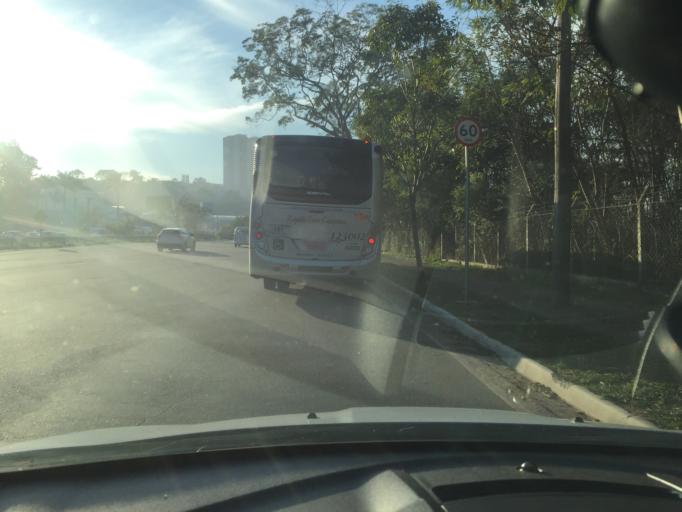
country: BR
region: Sao Paulo
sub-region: Jundiai
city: Jundiai
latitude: -23.1903
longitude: -46.8733
